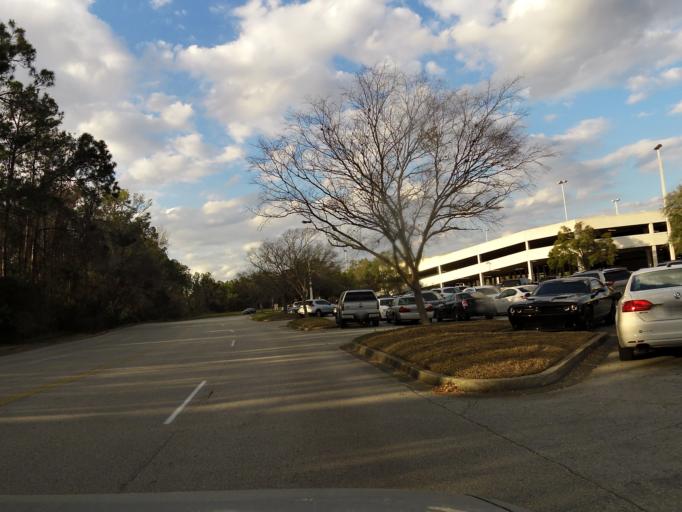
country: US
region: Florida
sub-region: Saint Johns County
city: Fruit Cove
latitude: 30.1856
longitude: -81.5557
